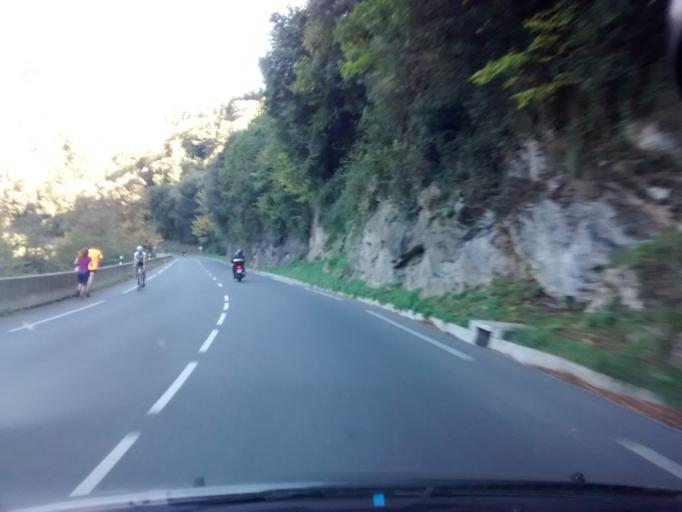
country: ES
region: Basque Country
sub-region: Provincia de Guipuzcoa
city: Deba
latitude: 43.2777
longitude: -2.3659
